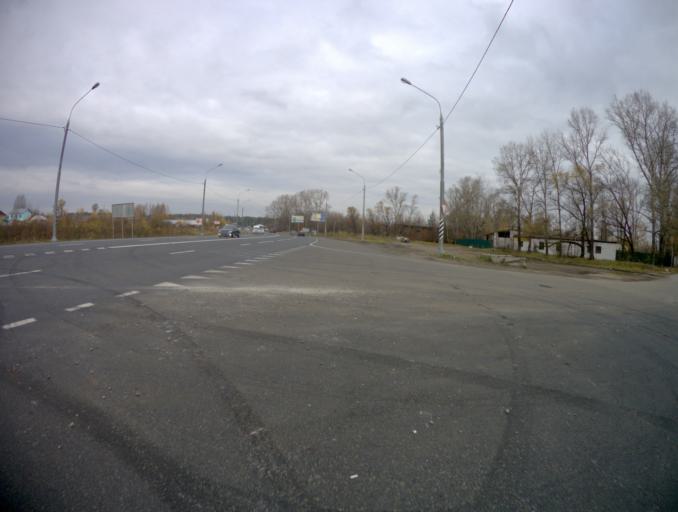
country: RU
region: Moskovskaya
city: Orekhovo-Zuyevo
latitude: 55.8400
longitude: 38.9702
